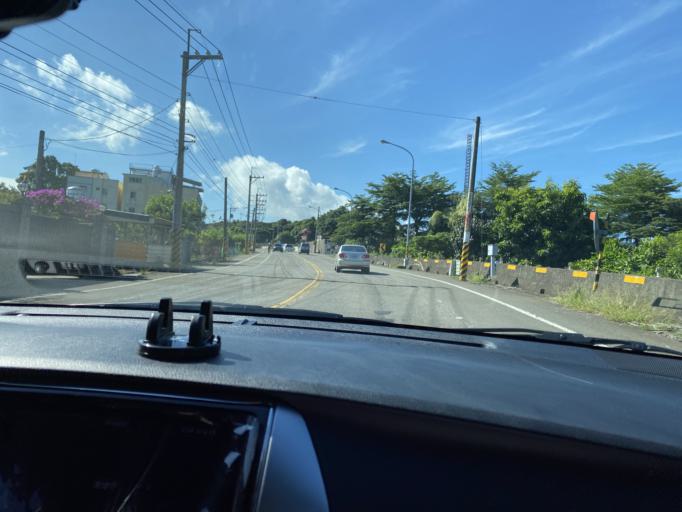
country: TW
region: Taiwan
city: Zhongxing New Village
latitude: 23.9687
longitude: 120.6244
